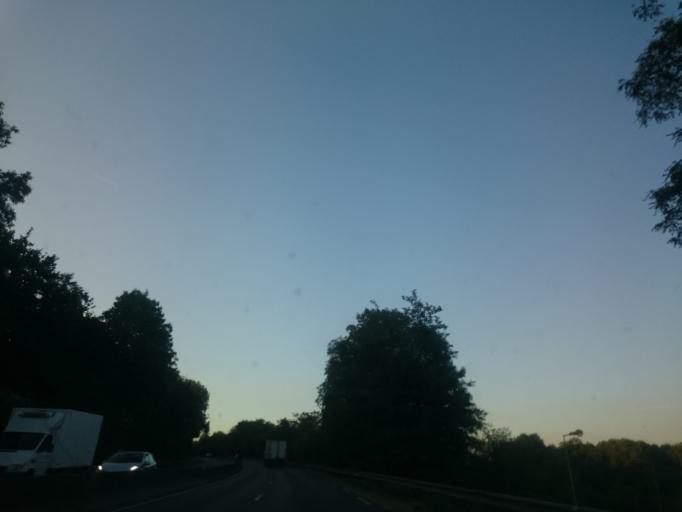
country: FR
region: Ile-de-France
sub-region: Departement de l'Essonne
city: Etrechy
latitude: 48.4971
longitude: 2.2010
